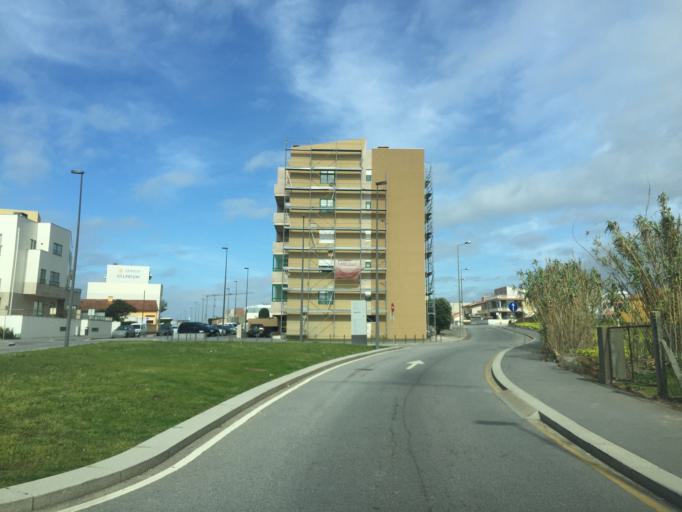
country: PT
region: Porto
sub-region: Matosinhos
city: Lavra
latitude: 41.2387
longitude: -8.7230
